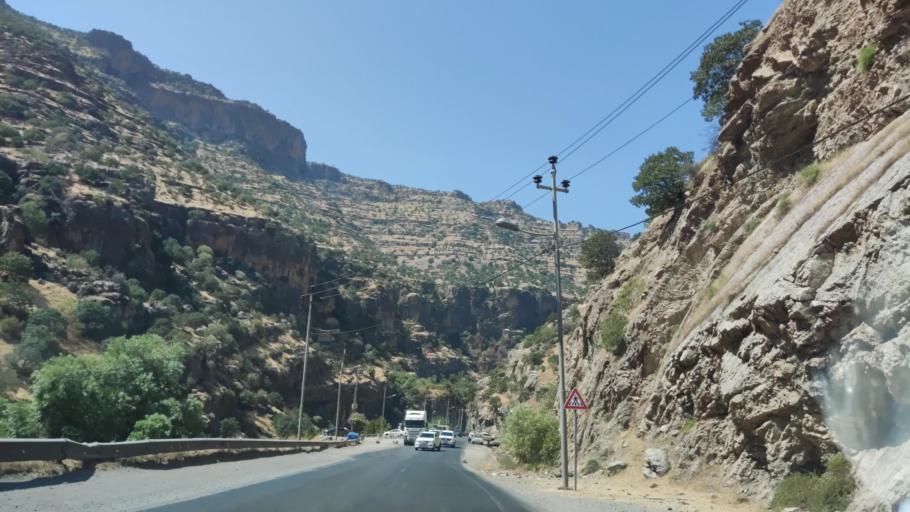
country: IQ
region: Arbil
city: Ruwandiz
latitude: 36.6290
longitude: 44.4712
